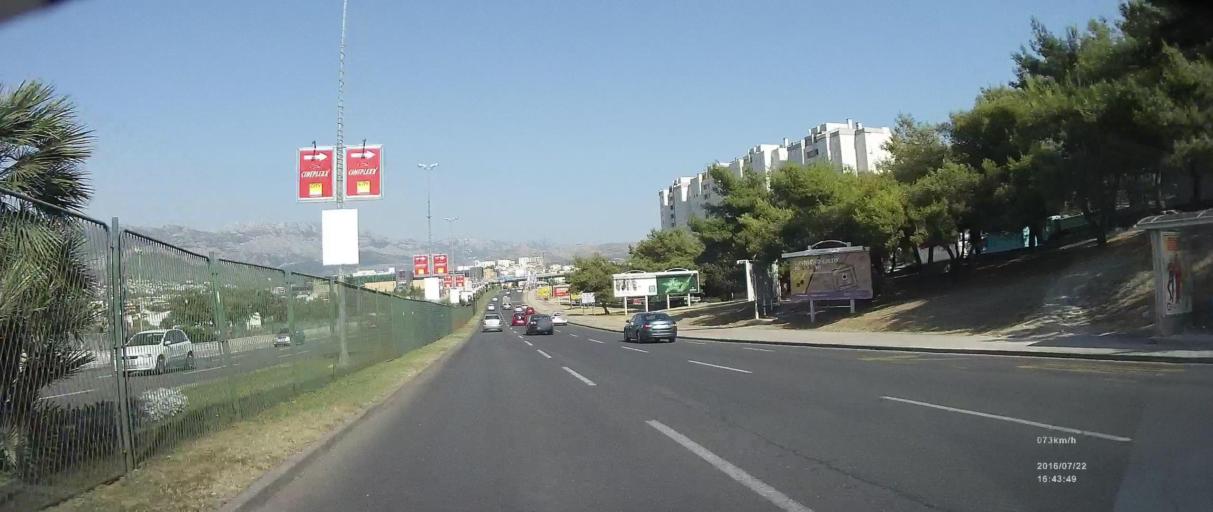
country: HR
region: Splitsko-Dalmatinska
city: Vranjic
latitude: 43.5190
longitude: 16.4750
